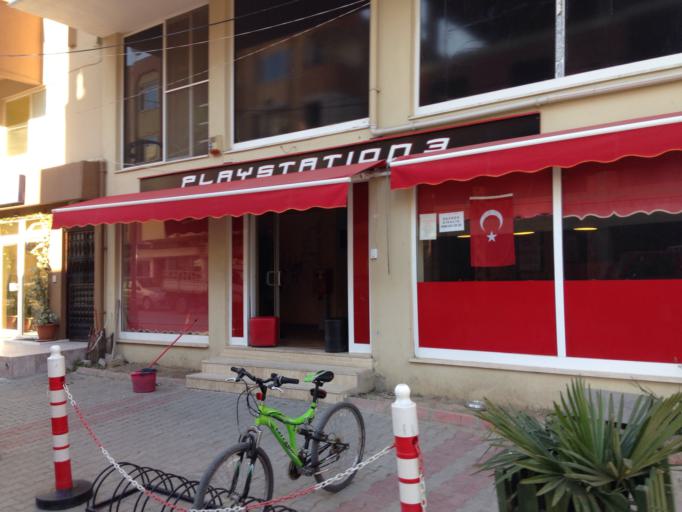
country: TR
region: Canakkale
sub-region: Merkez
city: Kucukkuyu
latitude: 39.5469
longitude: 26.6038
